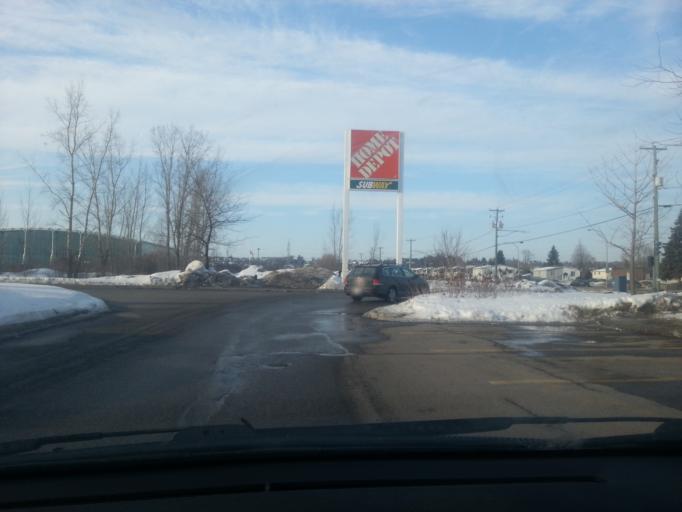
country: CA
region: Quebec
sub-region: Outaouais
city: Gatineau
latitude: 45.4847
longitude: -75.6754
